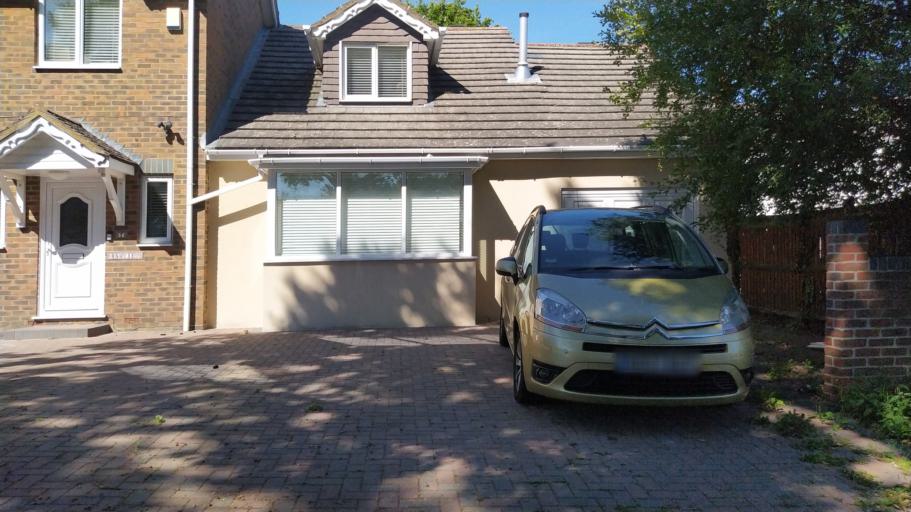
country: GB
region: England
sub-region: Hampshire
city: Totton
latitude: 50.9071
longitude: -1.4963
